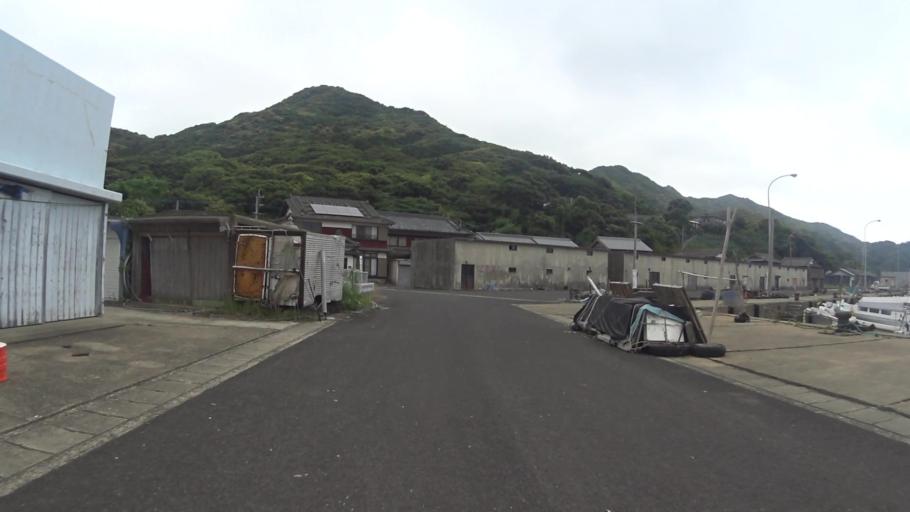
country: JP
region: Nagasaki
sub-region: Hirado Shi
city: Hirado
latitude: 33.1922
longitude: 129.3592
